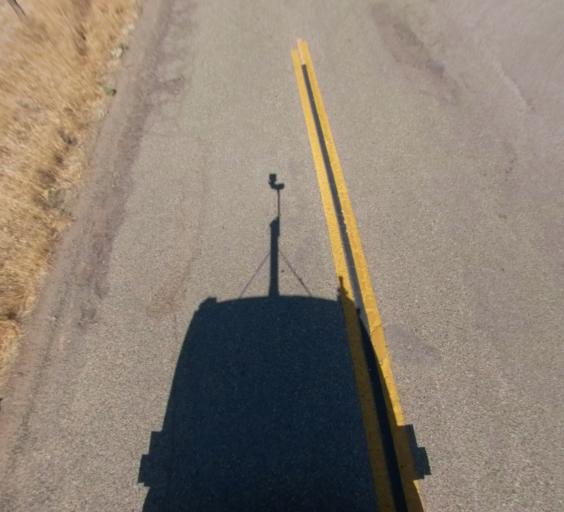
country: US
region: California
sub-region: Madera County
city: Bonadelle Ranchos-Madera Ranchos
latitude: 36.9959
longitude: -119.8648
